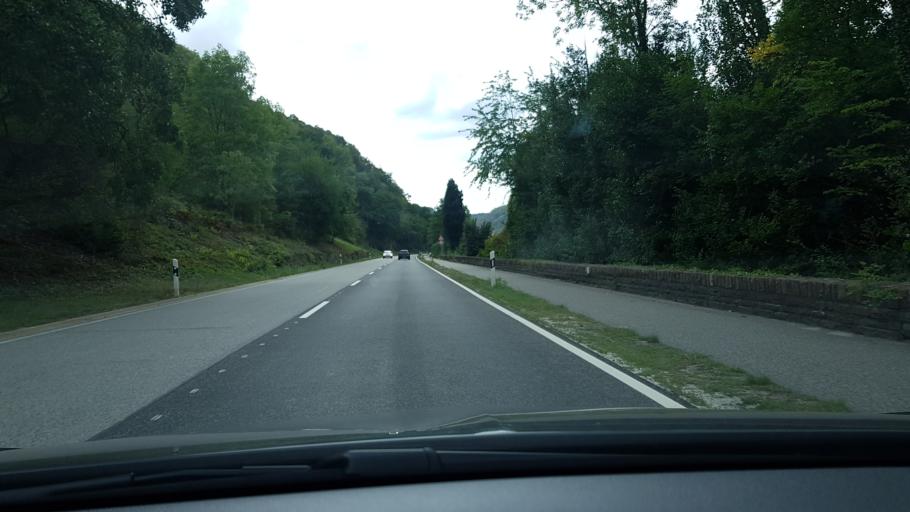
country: DE
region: Rheinland-Pfalz
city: Oberfell
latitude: 50.2681
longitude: 7.4558
